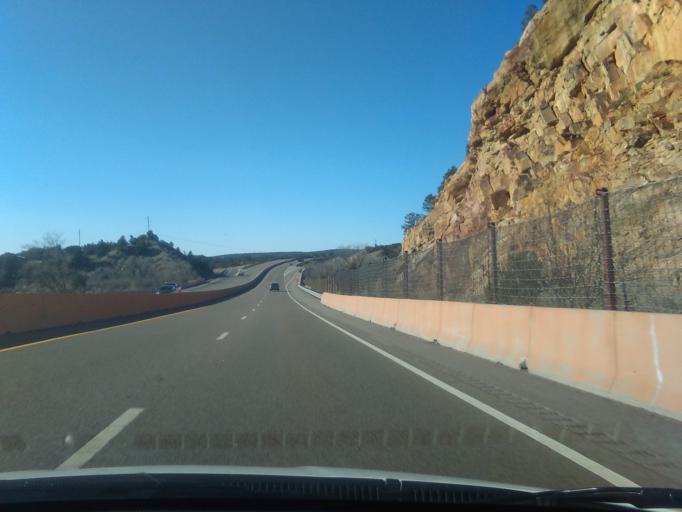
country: US
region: New Mexico
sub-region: Santa Fe County
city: Eldorado at Santa Fe
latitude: 35.5509
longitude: -105.8233
